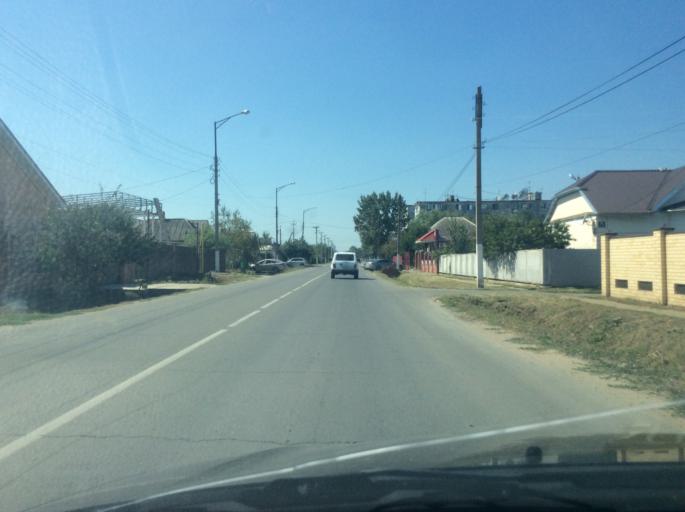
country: RU
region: Krasnodarskiy
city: Slavyansk-na-Kubani
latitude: 45.2519
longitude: 38.1121
